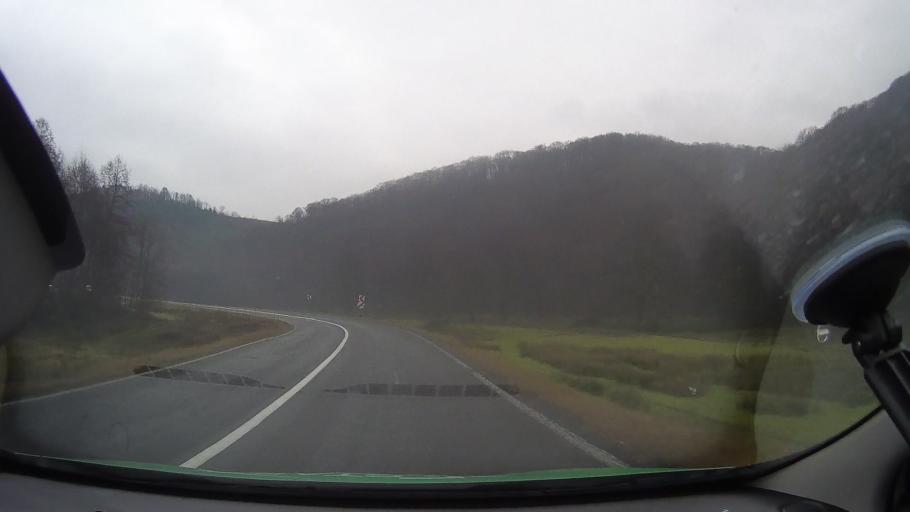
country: RO
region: Arad
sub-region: Comuna Plescuta
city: Plescuta
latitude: 46.3160
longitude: 22.4680
